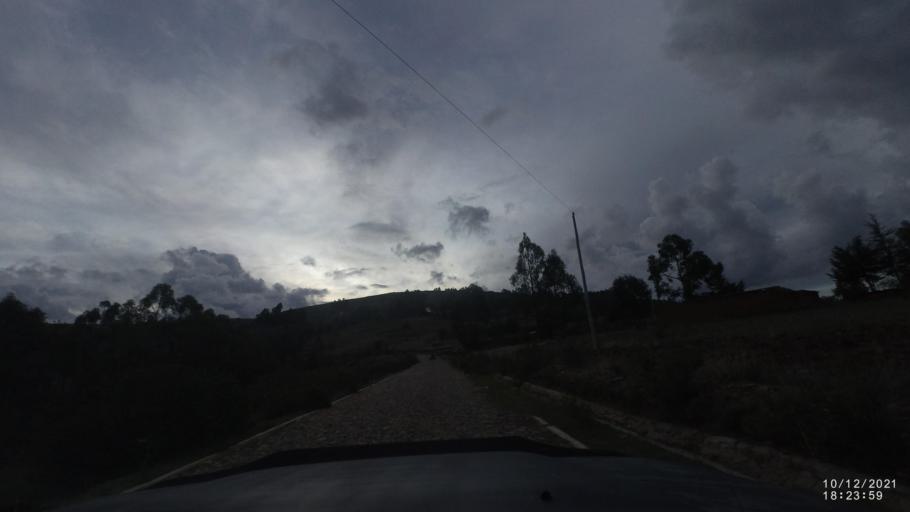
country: BO
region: Cochabamba
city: Tarata
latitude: -17.7874
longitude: -65.9714
